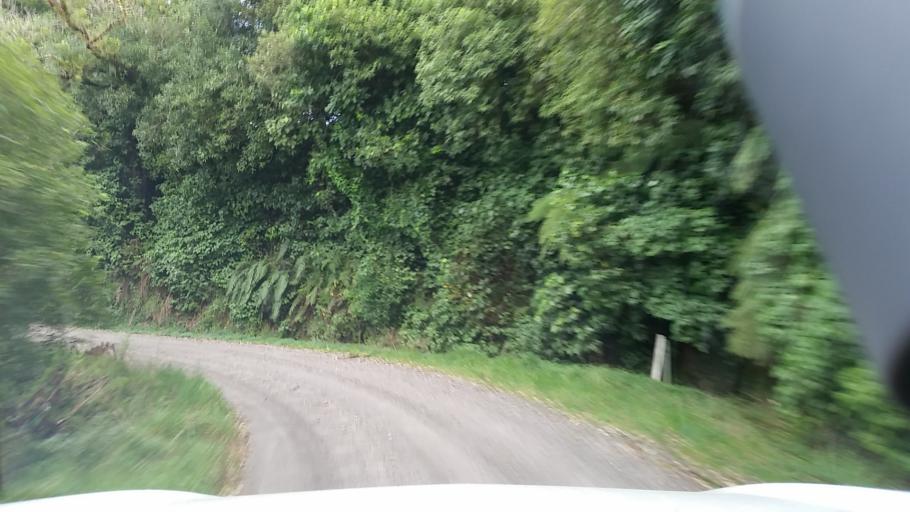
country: NZ
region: Bay of Plenty
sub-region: Rotorua District
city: Rotorua
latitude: -37.9643
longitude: 176.3065
